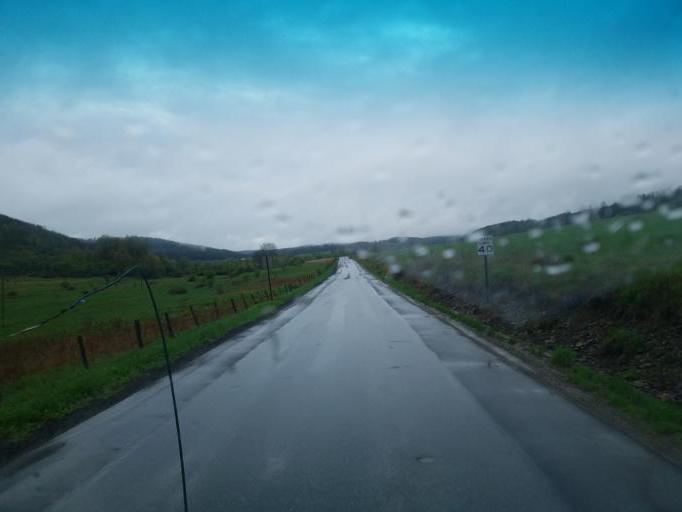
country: US
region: Pennsylvania
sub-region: Tioga County
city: Westfield
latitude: 41.9652
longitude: -77.6525
